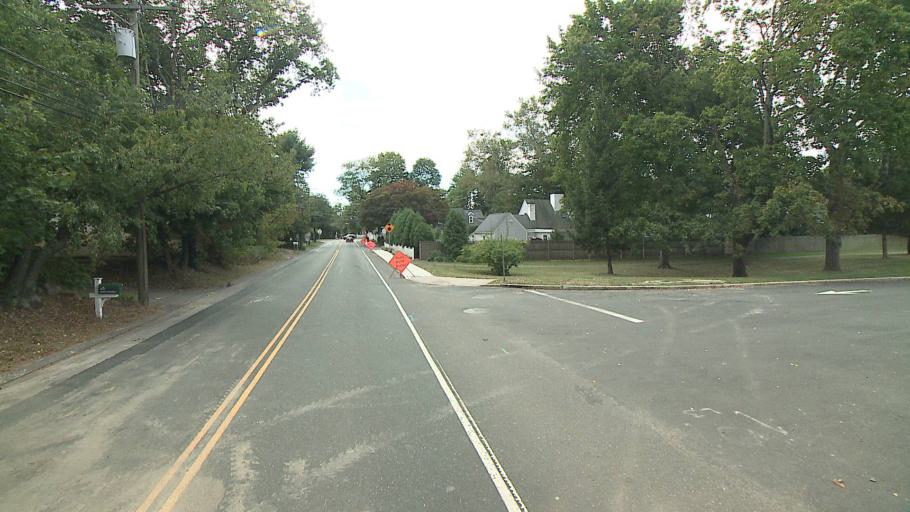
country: US
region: Connecticut
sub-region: Fairfield County
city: Stamford
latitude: 41.0789
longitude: -73.5121
